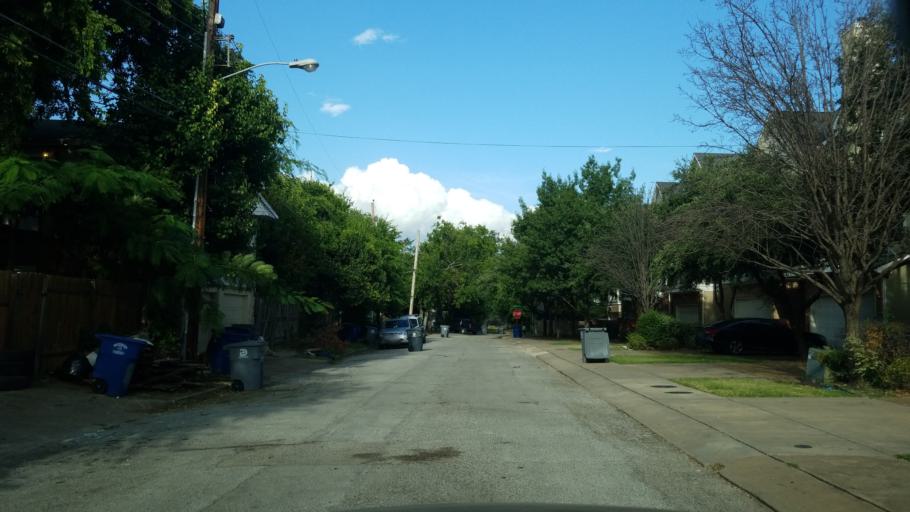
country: US
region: Texas
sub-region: Dallas County
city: Highland Park
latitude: 32.8127
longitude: -96.7679
